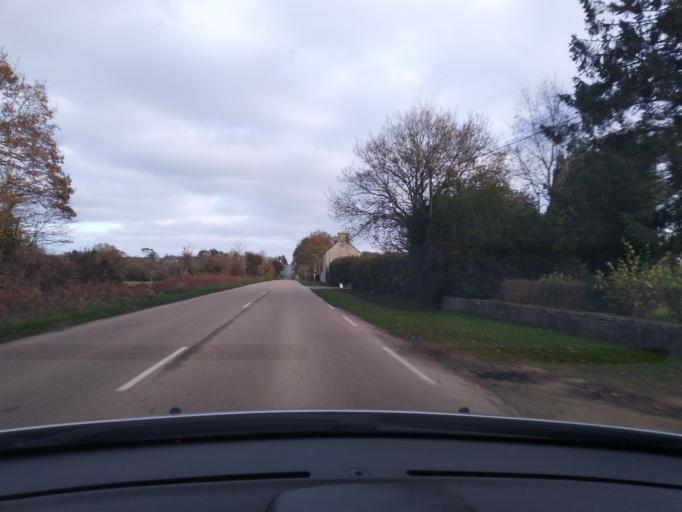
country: FR
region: Brittany
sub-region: Departement du Finistere
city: Plourin-les-Morlaix
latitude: 48.5766
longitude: -3.7751
